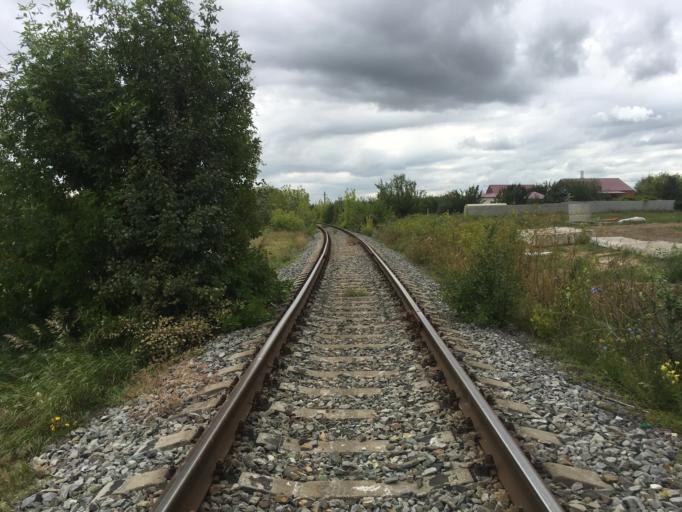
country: RU
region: Voronezj
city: Rossosh'
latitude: 50.2126
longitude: 39.5204
